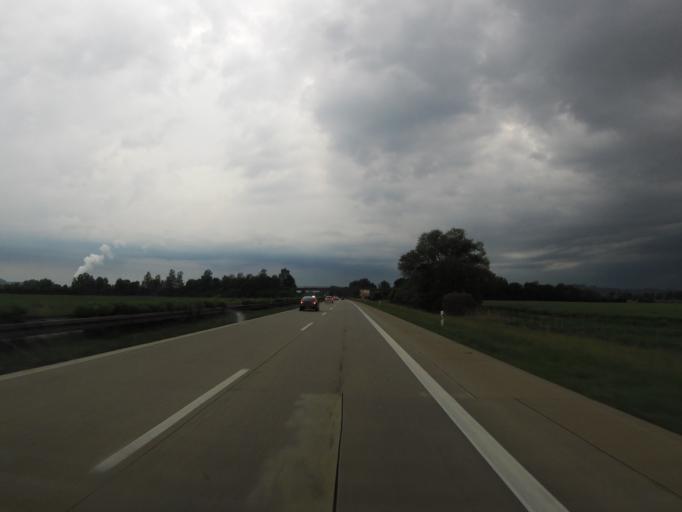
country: DE
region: Bavaria
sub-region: Lower Bavaria
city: Worth an der Isar
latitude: 48.6351
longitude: 12.3566
